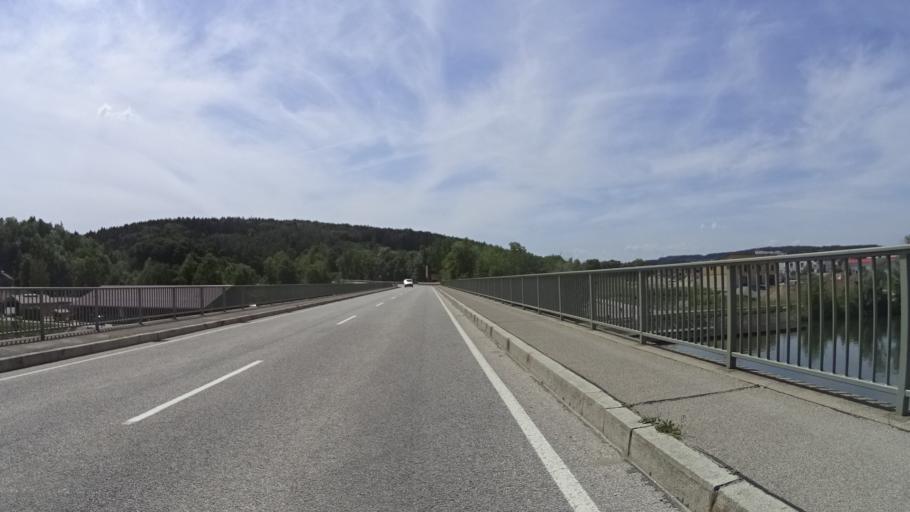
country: DE
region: Bavaria
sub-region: Lower Bavaria
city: Bad Abbach
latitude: 48.9269
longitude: 12.0135
